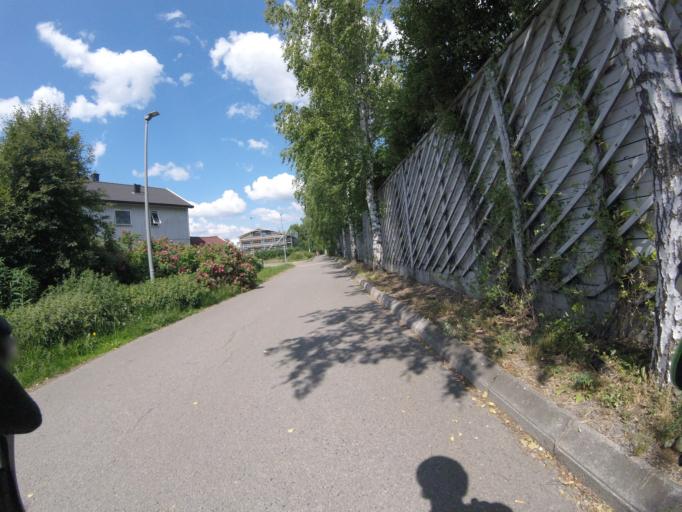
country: NO
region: Akershus
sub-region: Skedsmo
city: Lillestrom
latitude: 59.9596
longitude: 11.0657
